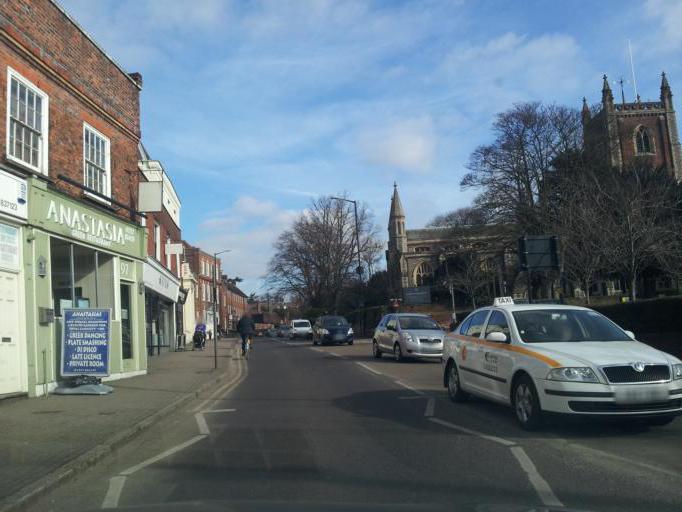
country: GB
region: England
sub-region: Hertfordshire
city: St Albans
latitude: 51.7550
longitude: -0.3359
